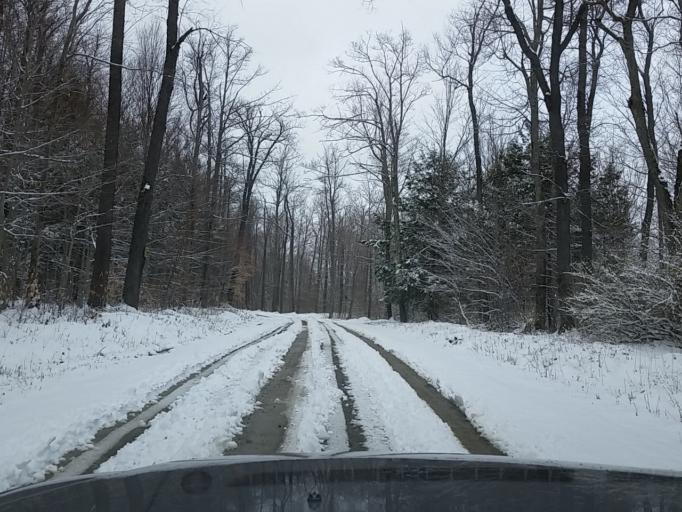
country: US
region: Pennsylvania
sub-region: Sullivan County
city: Laporte
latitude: 41.3499
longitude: -76.4612
